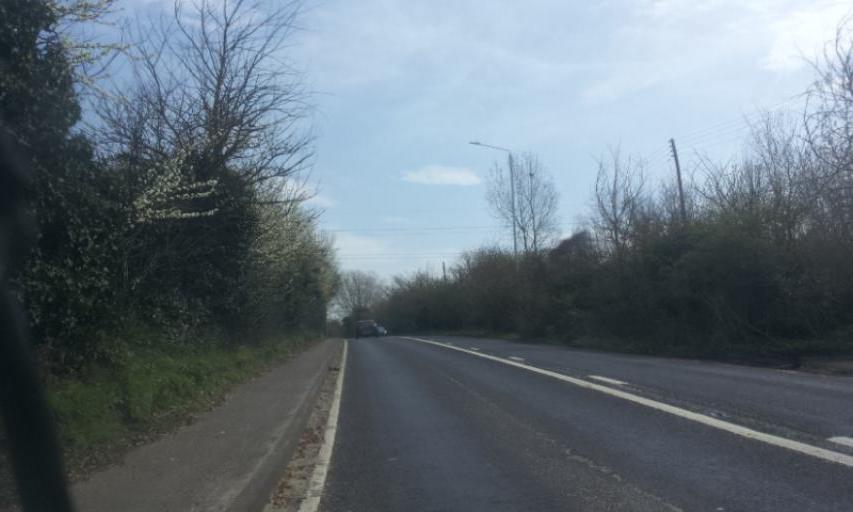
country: GB
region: England
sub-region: Kent
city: Rainham
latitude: 51.3581
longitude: 0.6351
